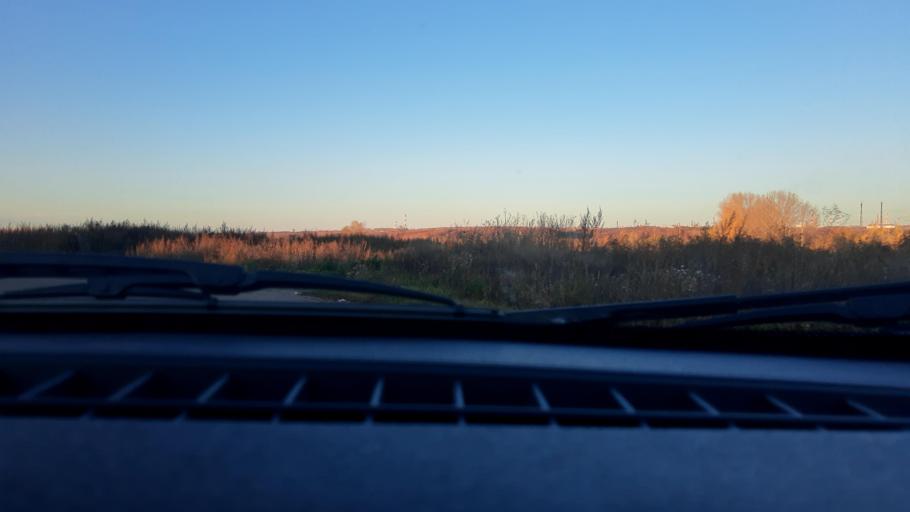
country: RU
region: Bashkortostan
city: Ufa
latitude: 54.8582
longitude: 56.0227
